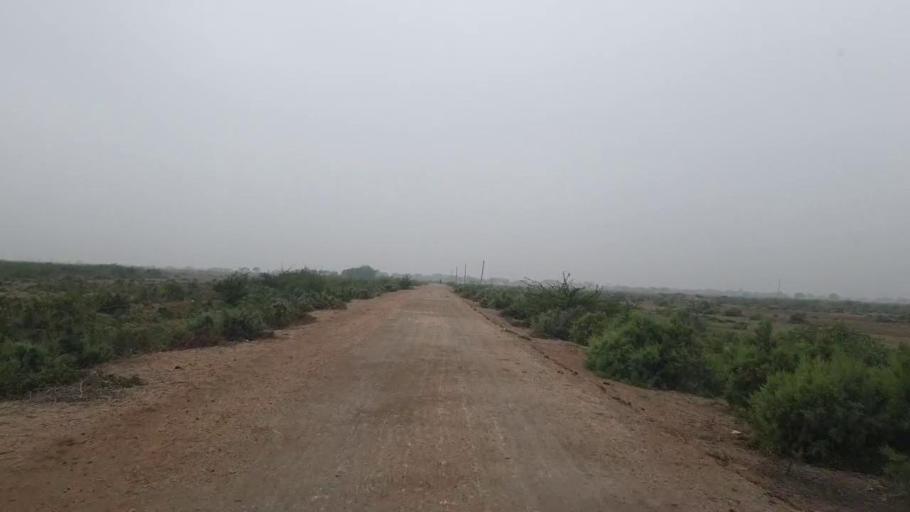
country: PK
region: Sindh
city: Badin
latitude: 24.6009
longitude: 68.6687
